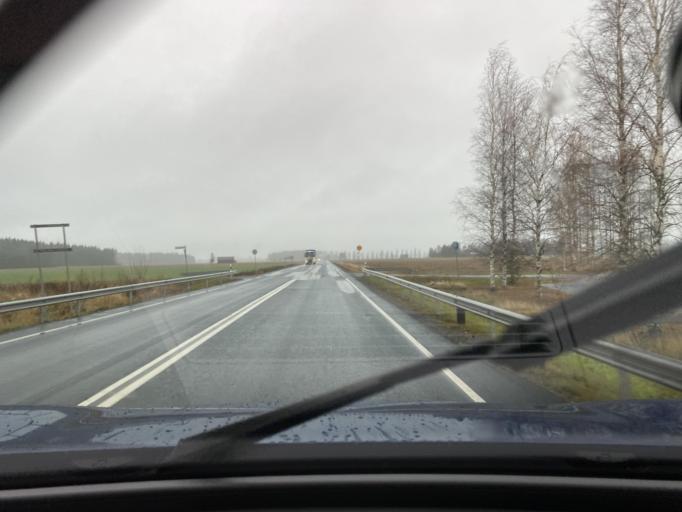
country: FI
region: Varsinais-Suomi
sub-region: Loimaa
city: Alastaro
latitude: 60.8915
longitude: 22.9659
